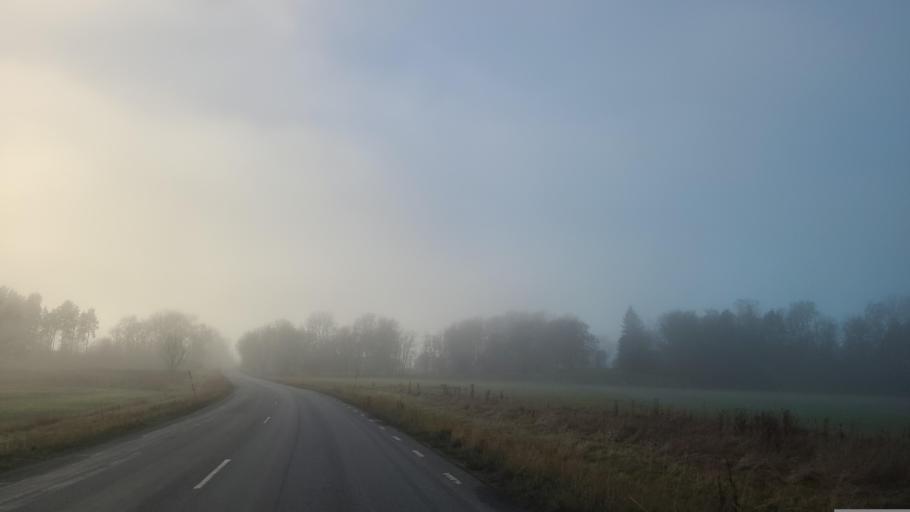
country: SE
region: Uppsala
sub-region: Enkopings Kommun
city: Grillby
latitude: 59.5959
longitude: 17.2312
